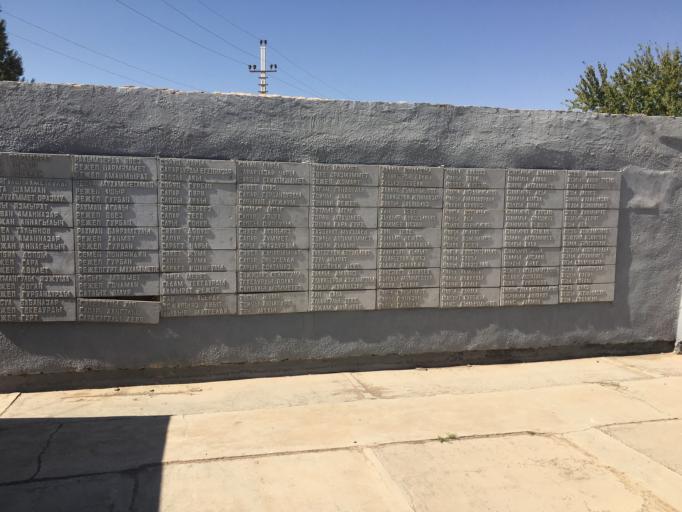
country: IR
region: Razavi Khorasan
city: Sarakhs
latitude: 36.5292
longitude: 61.2123
